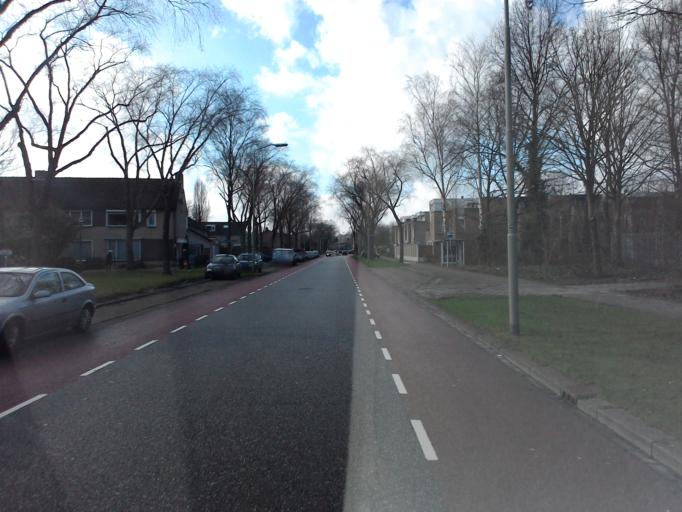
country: NL
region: North Brabant
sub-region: Gemeente Boxtel
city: Boxtel
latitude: 51.5866
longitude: 5.3372
